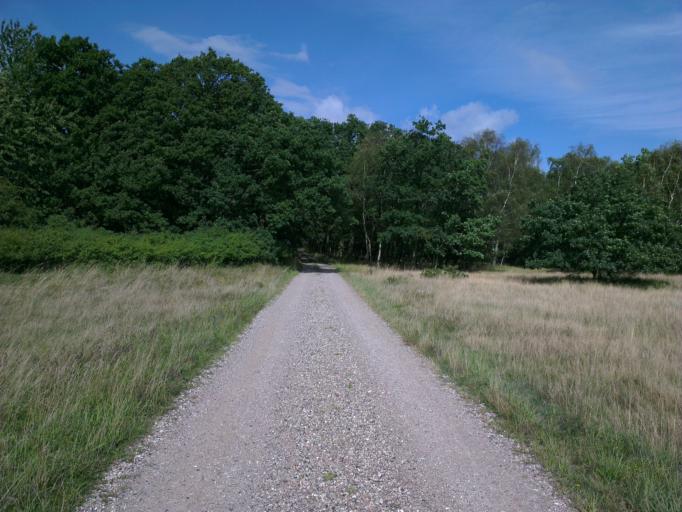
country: DK
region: Capital Region
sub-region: Frederikssund Kommune
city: Jaegerspris
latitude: 55.8450
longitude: 11.9633
